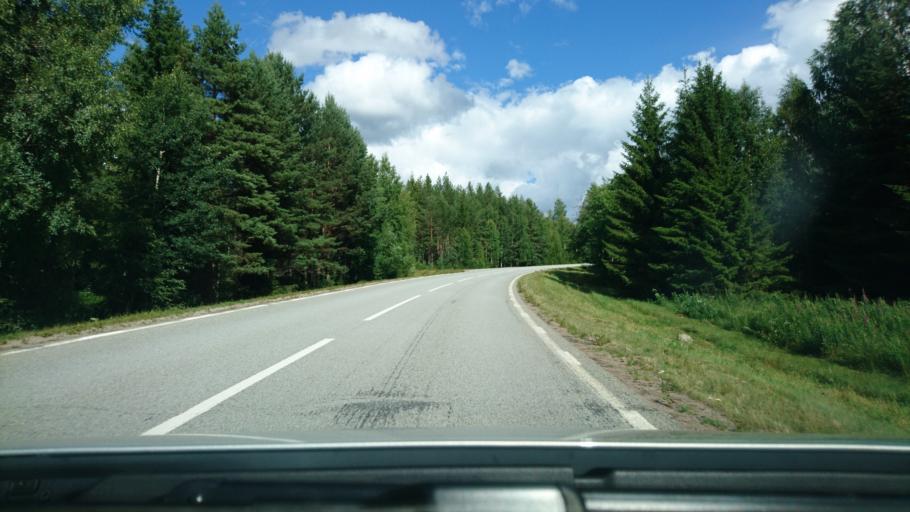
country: SE
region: Vaesternorrland
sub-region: Solleftea Kommun
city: As
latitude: 63.7179
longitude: 16.9536
